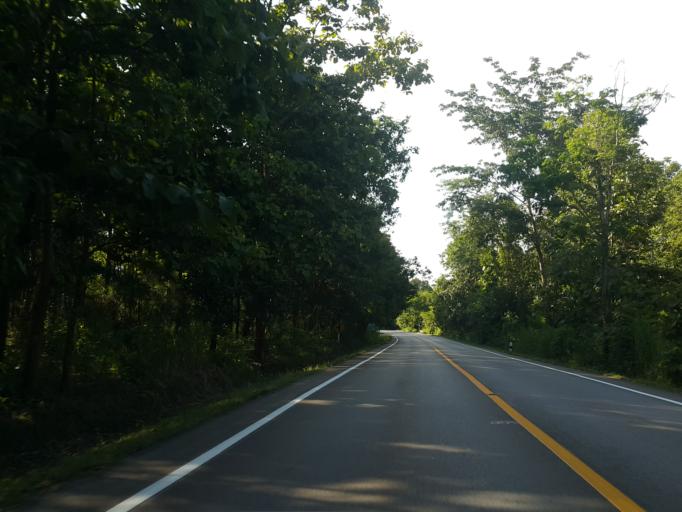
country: TH
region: Chiang Mai
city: Mae Taeng
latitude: 19.0814
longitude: 99.1028
